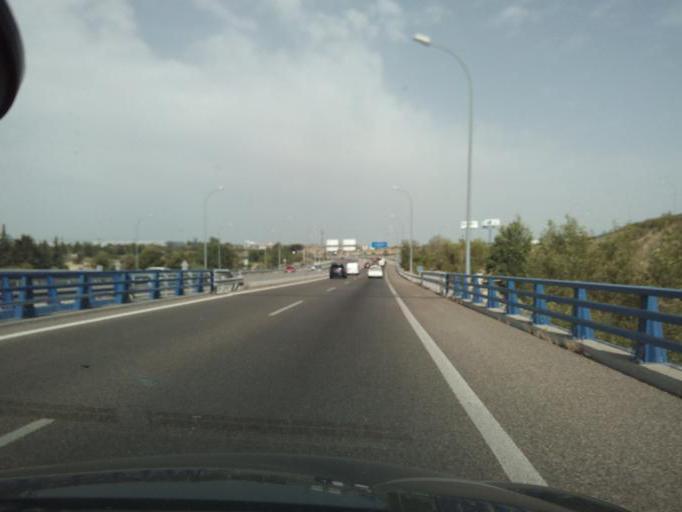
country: ES
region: Madrid
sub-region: Provincia de Madrid
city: Barajas de Madrid
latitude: 40.4704
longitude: -3.6029
